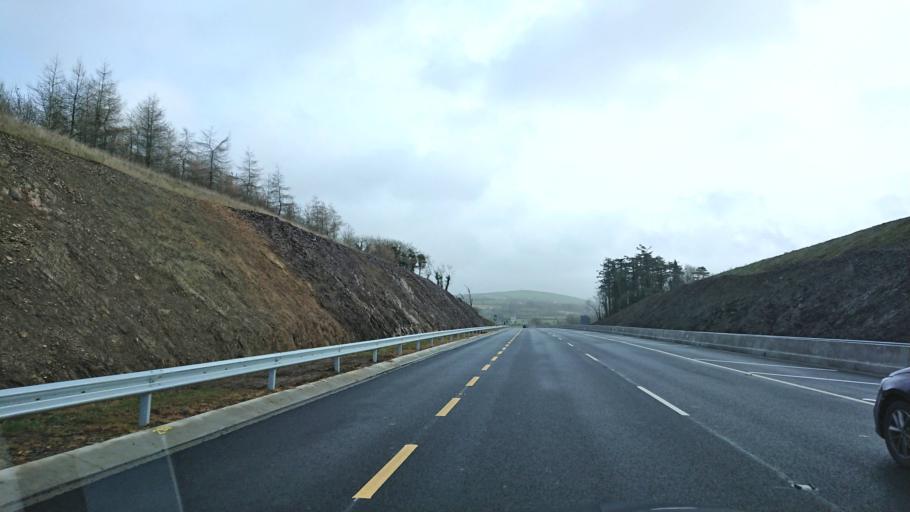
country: IE
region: Leinster
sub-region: Loch Garman
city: New Ross
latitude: 52.3605
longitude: -6.9744
